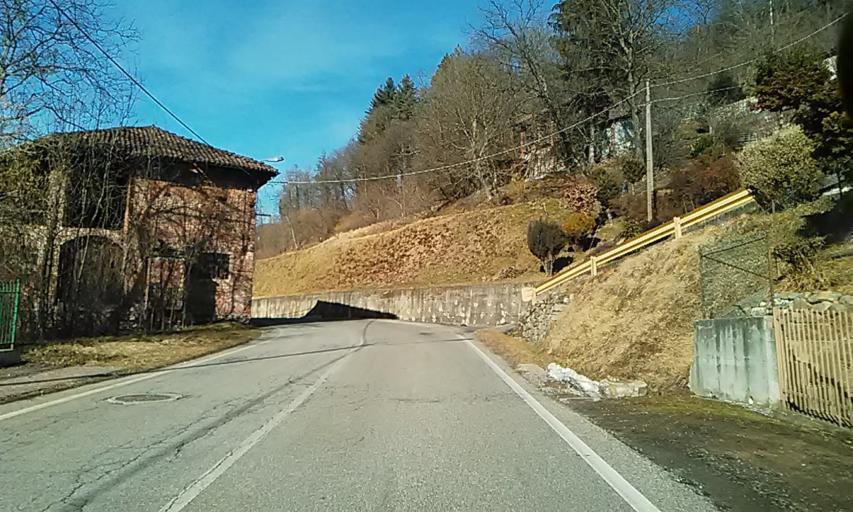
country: IT
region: Piedmont
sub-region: Provincia di Vercelli
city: Valduggia
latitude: 45.7280
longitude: 8.3014
